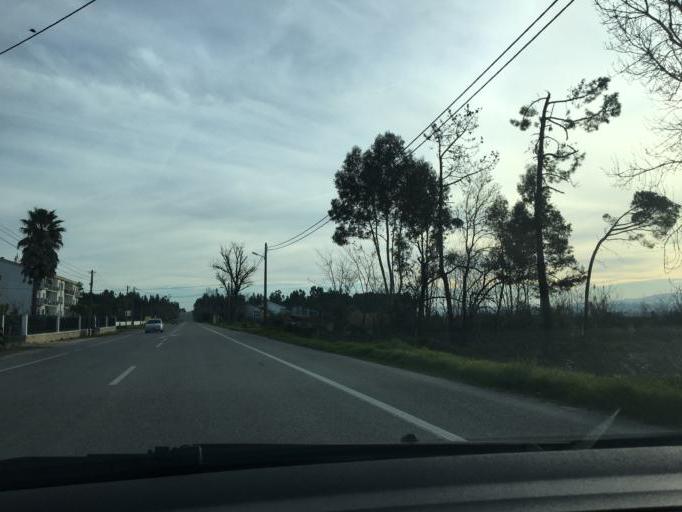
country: PT
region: Coimbra
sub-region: Soure
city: Alfarelos
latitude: 40.2117
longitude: -8.6154
